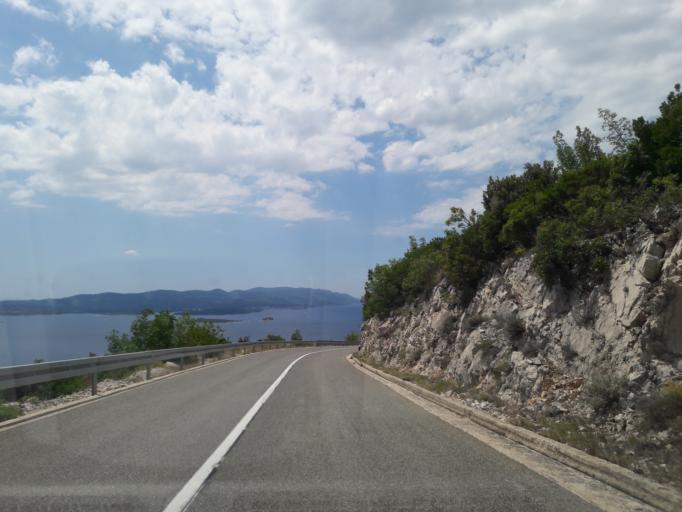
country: HR
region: Dubrovacko-Neretvanska
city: Orebic
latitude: 42.9698
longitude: 17.2515
